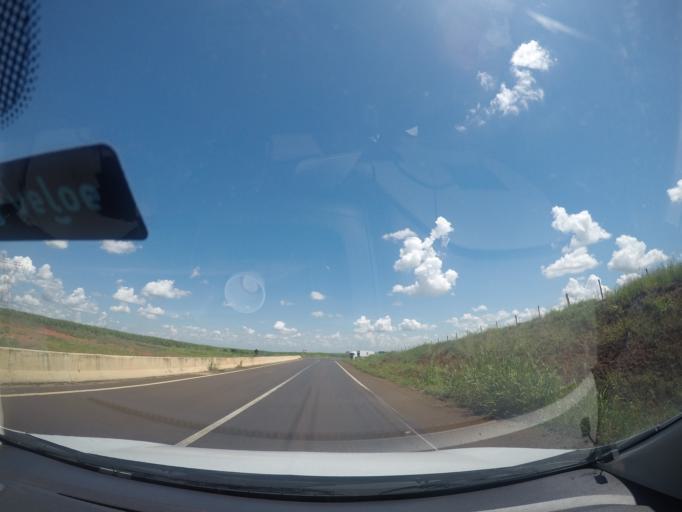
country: BR
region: Minas Gerais
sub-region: Frutal
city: Frutal
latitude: -19.6994
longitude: -48.7652
